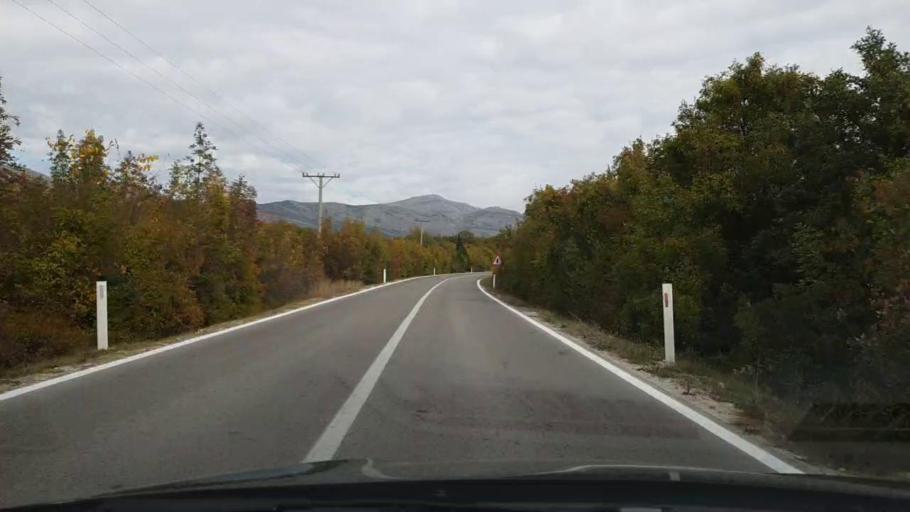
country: BA
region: Republika Srpska
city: Trebinje
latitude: 42.6887
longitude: 18.2534
